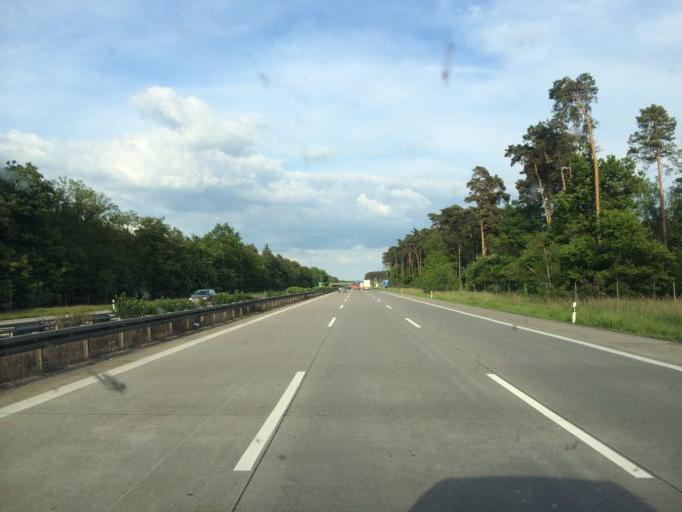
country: DE
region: Saxony-Anhalt
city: Mockern
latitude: 52.2353
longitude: 11.9586
